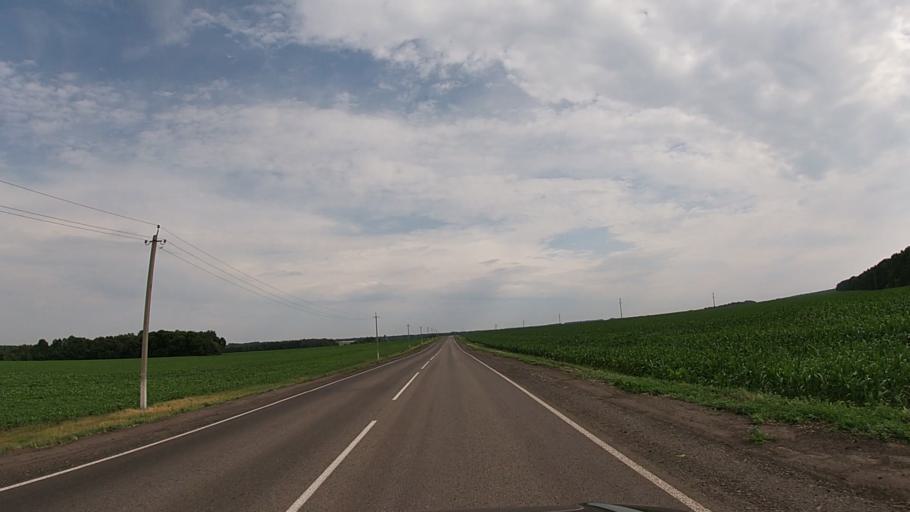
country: RU
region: Belgorod
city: Krasnaya Yaruga
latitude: 50.8148
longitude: 35.5017
